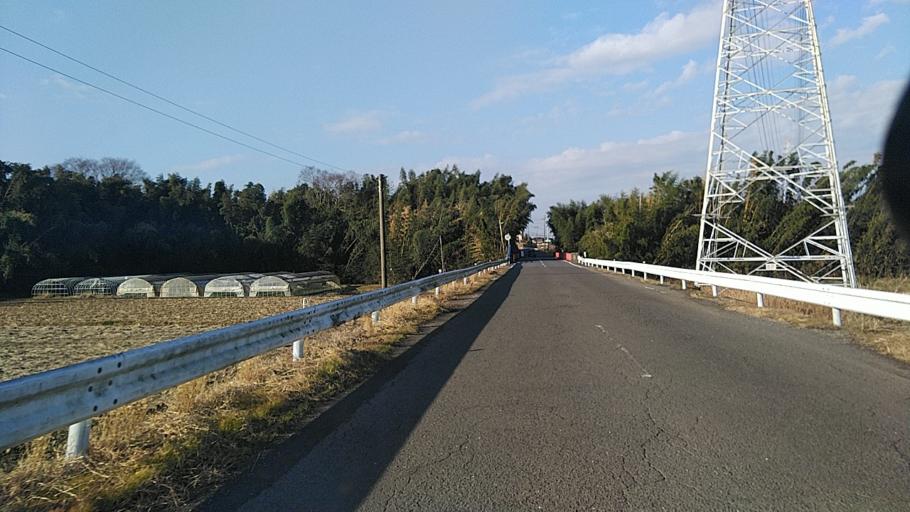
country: JP
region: Chiba
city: Kimitsu
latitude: 35.3063
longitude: 139.9738
